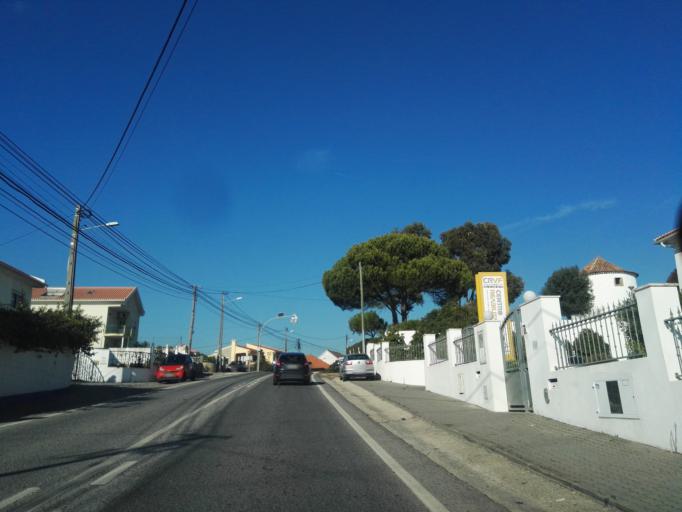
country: PT
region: Lisbon
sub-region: Loures
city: Loures
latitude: 38.8462
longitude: -9.1803
